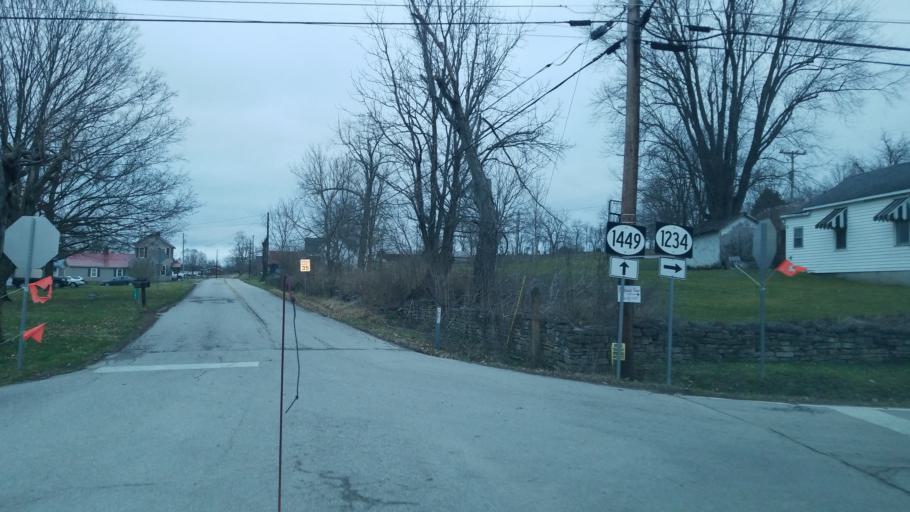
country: US
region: Kentucky
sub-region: Mason County
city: Maysville
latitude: 38.5668
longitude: -83.6893
